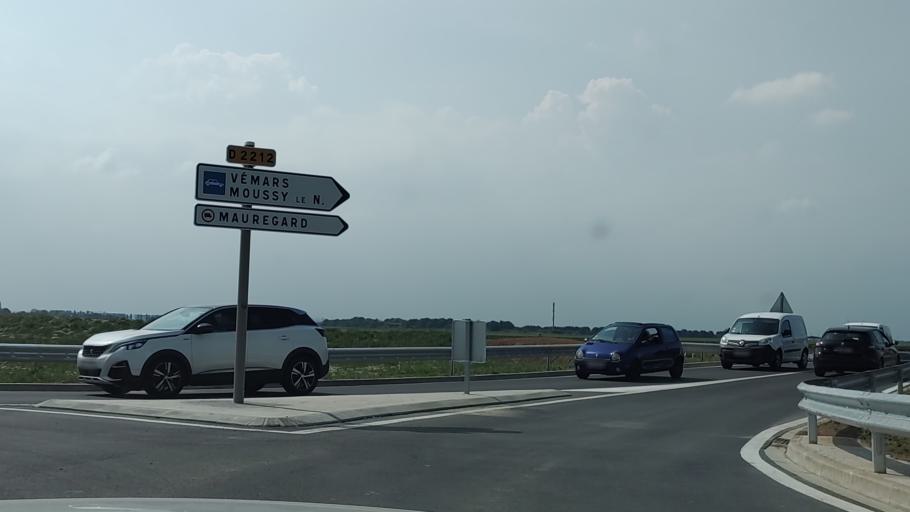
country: FR
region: Ile-de-France
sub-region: Departement de Seine-et-Marne
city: Moussy-le-Neuf
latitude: 49.0294
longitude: 2.5820
